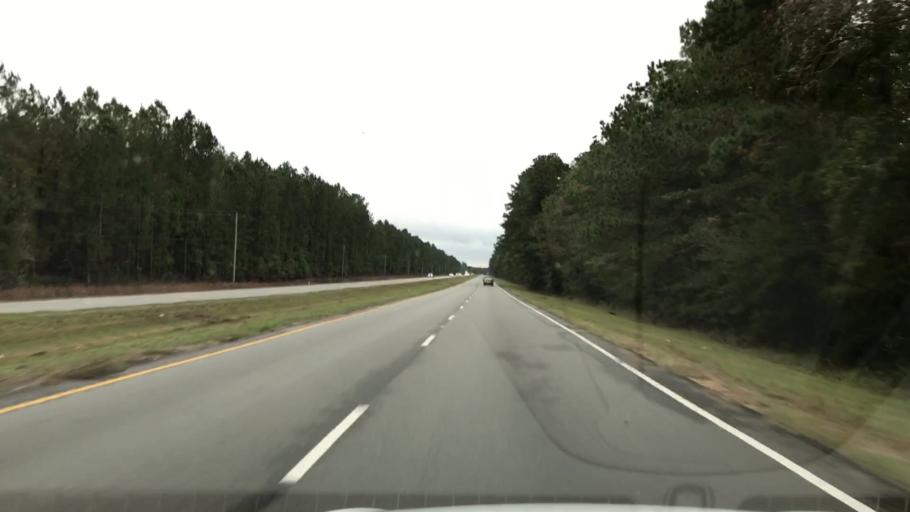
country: US
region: South Carolina
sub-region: Georgetown County
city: Georgetown
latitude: 33.2769
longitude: -79.3516
